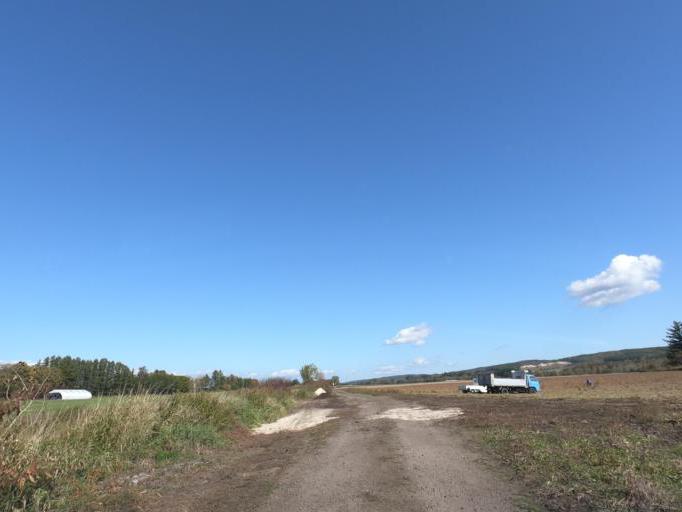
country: JP
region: Hokkaido
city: Otofuke
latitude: 43.0610
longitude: 143.2773
